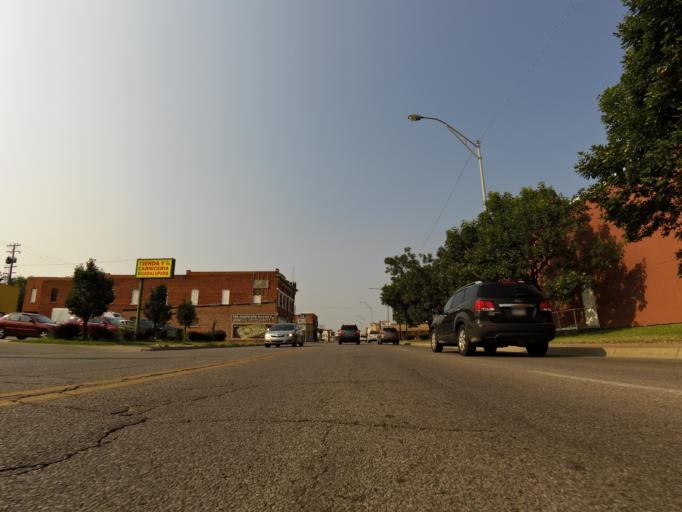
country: US
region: Kansas
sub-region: Sedgwick County
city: Wichita
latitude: 37.7164
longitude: -97.3356
